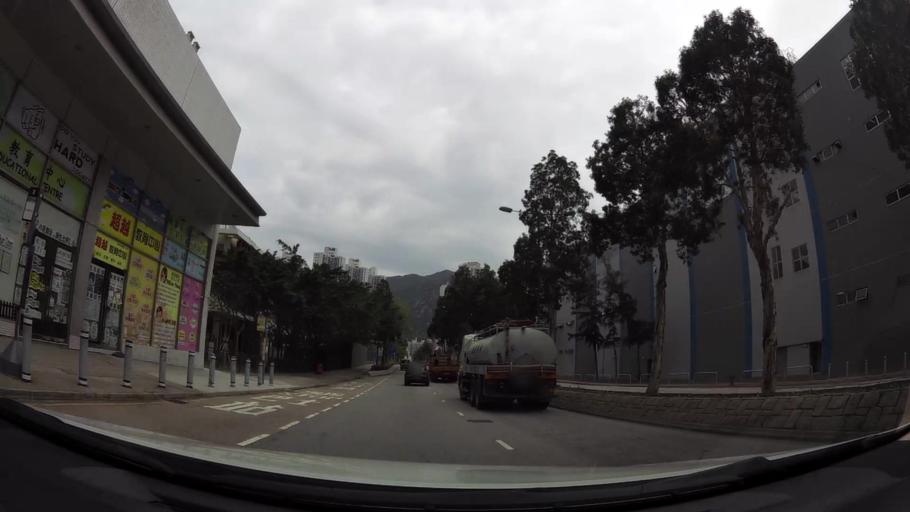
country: HK
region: Tuen Mun
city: Tuen Mun
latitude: 22.3813
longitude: 113.9724
